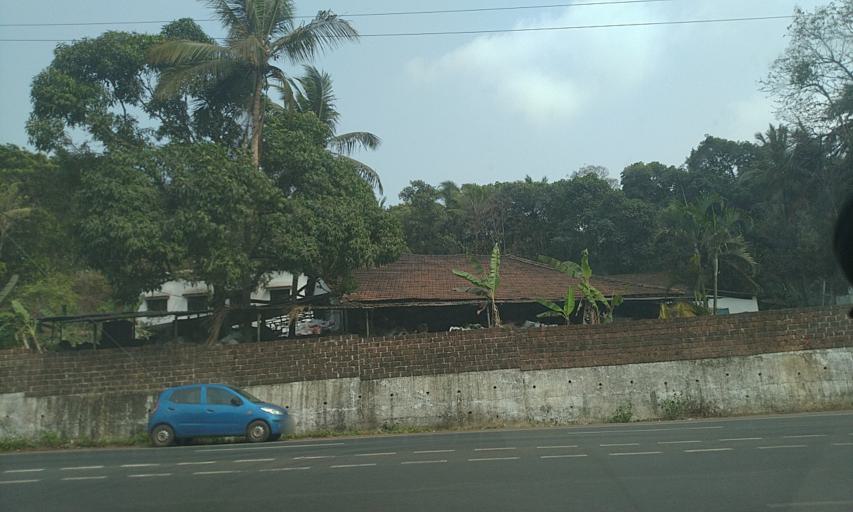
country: IN
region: Goa
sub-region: South Goa
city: Raia
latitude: 15.3081
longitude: 73.9775
